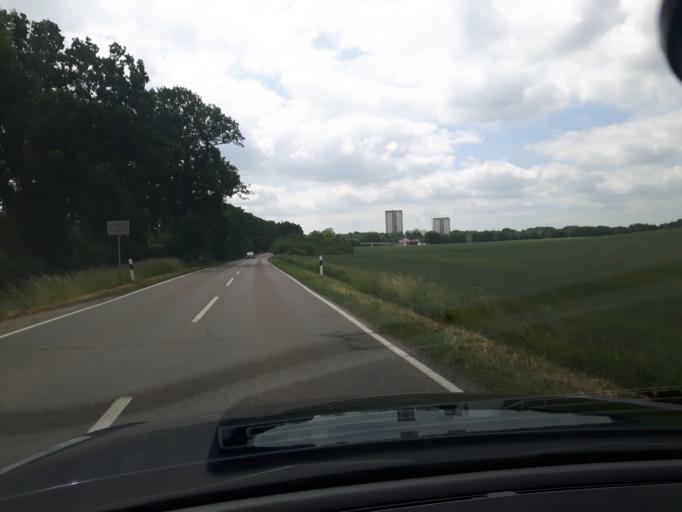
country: DE
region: Schleswig-Holstein
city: Sierksdorf
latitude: 54.0799
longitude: 10.7765
